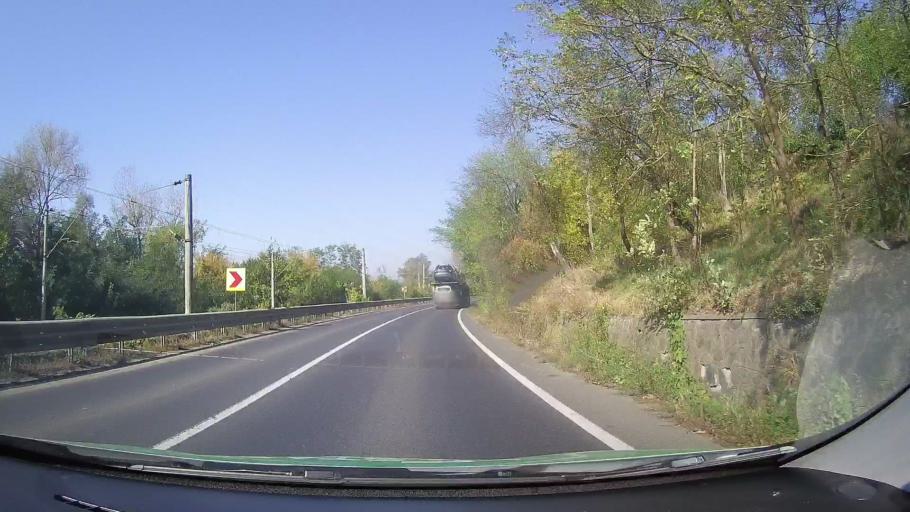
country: RO
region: Arad
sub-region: Comuna Bata
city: Bata
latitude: 46.0380
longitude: 22.0605
